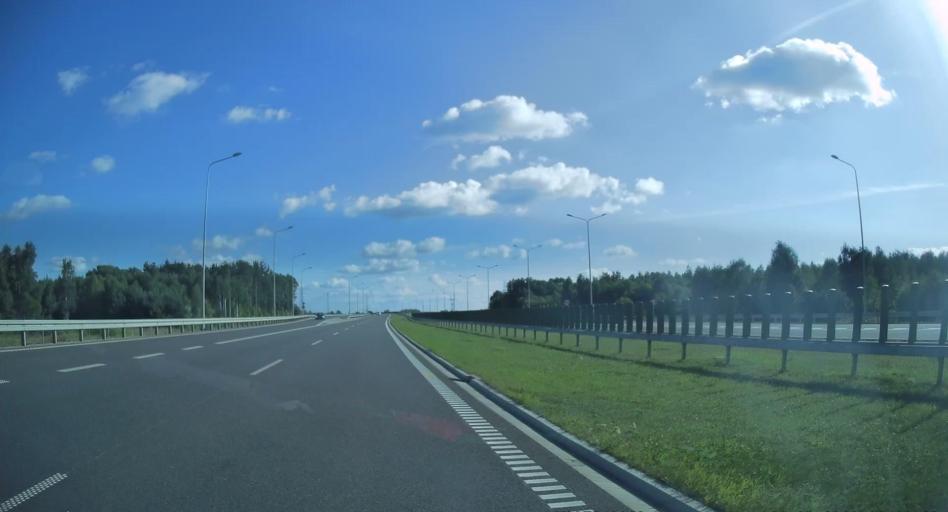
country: PL
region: Masovian Voivodeship
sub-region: Powiat szydlowiecki
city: Oronsko
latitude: 51.3414
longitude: 21.0153
